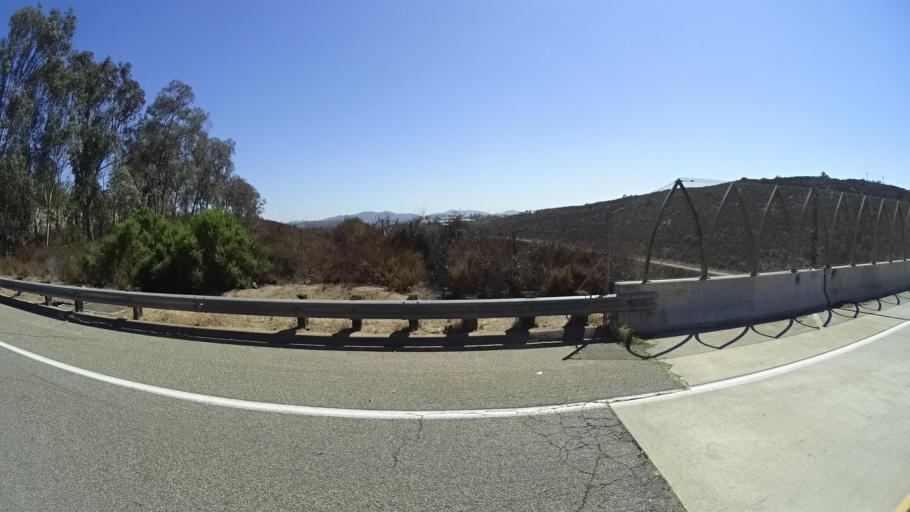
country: US
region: California
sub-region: San Diego County
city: Bonsall
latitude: 33.3000
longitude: -117.1491
